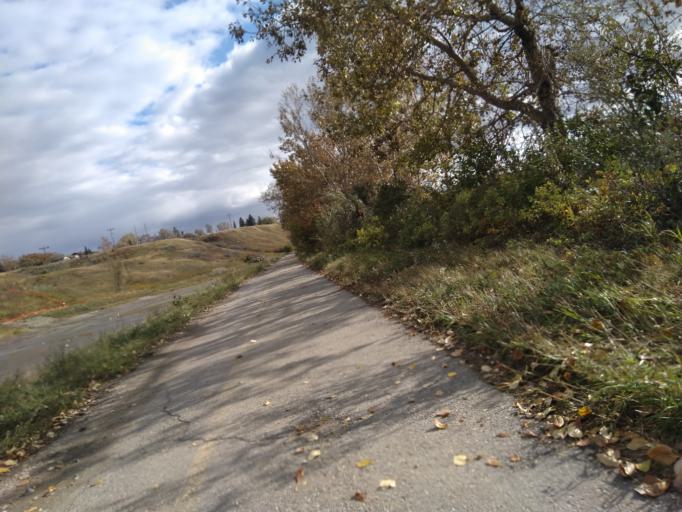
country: CA
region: Alberta
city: Calgary
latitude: 51.0354
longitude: -113.9993
